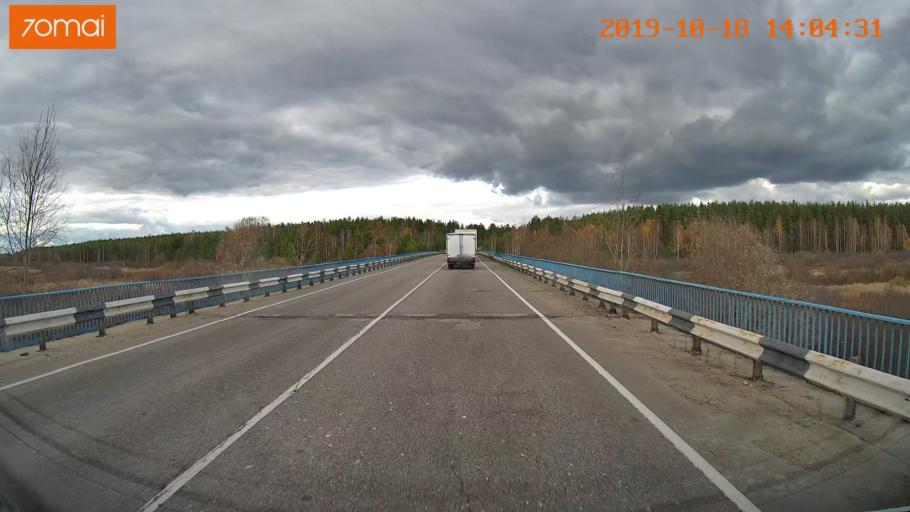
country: RU
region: Rjazan
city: Spas-Klepiki
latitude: 55.1267
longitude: 40.1335
